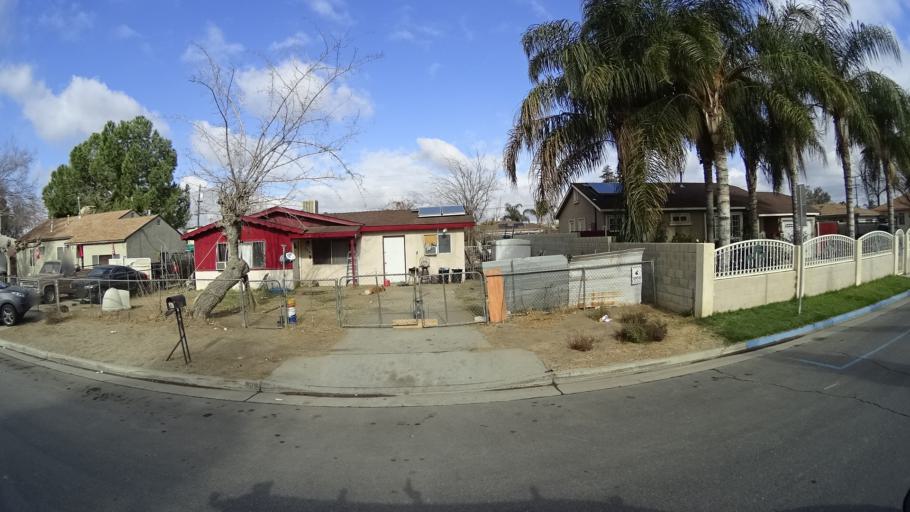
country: US
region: California
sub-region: Kern County
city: Bakersfield
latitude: 35.3295
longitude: -118.9889
